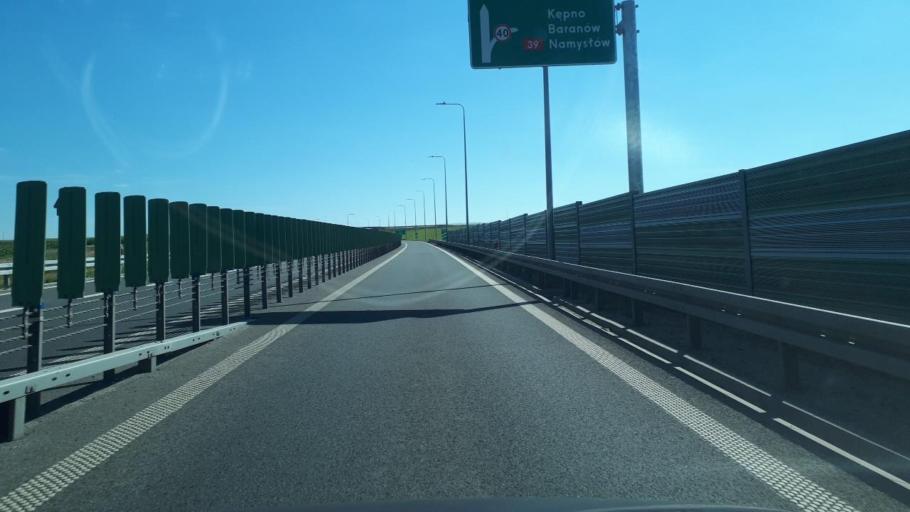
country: PL
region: Greater Poland Voivodeship
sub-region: Powiat kepinski
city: Baranow
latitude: 51.2601
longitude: 18.0175
